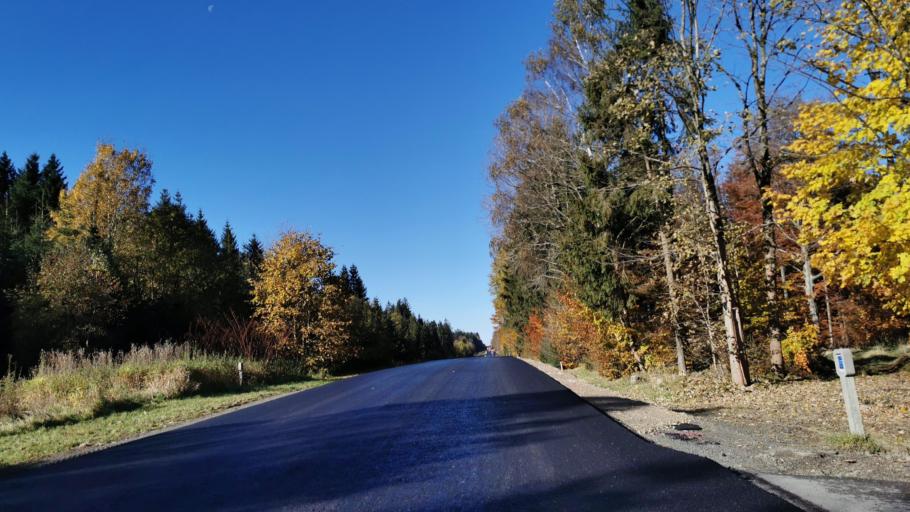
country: DE
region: Thuringia
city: Wurzbach
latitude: 50.4194
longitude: 11.5277
